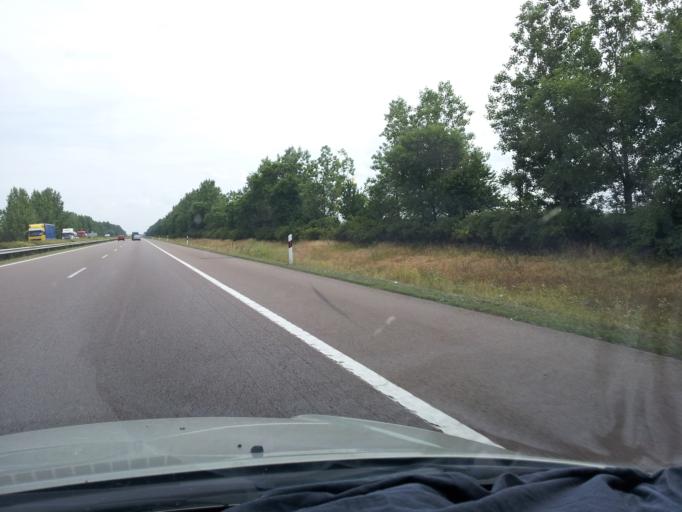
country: HU
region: Borsod-Abauj-Zemplen
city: Mezokovesd
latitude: 47.7829
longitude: 20.6017
